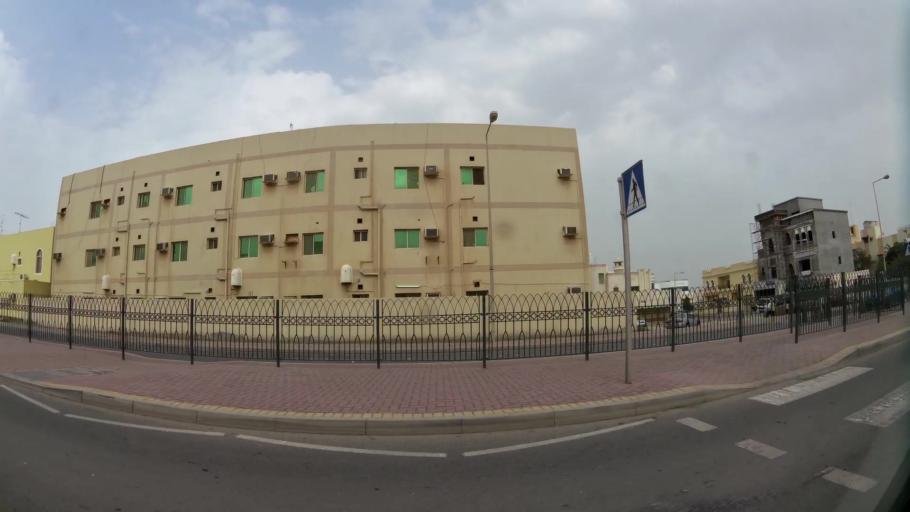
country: BH
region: Northern
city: Ar Rifa'
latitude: 26.1338
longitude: 50.5611
